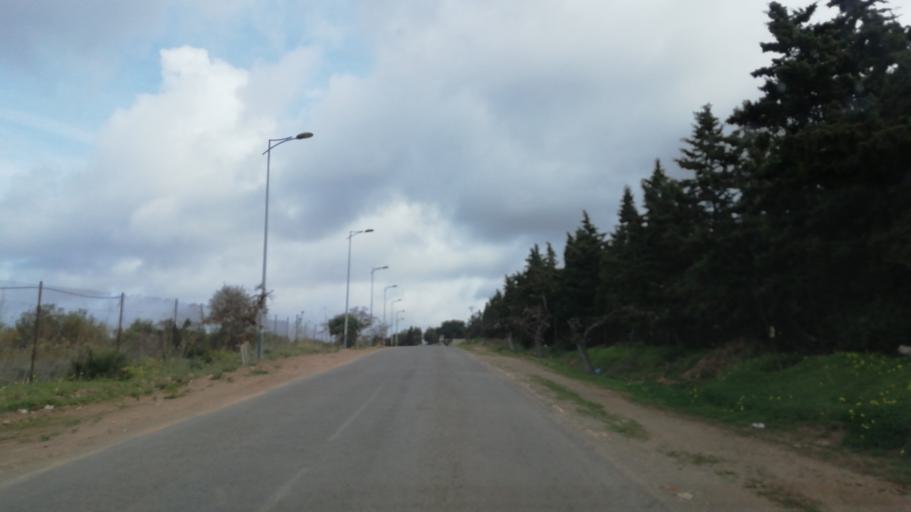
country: DZ
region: Oran
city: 'Ain el Turk
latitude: 35.6960
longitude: -0.8541
